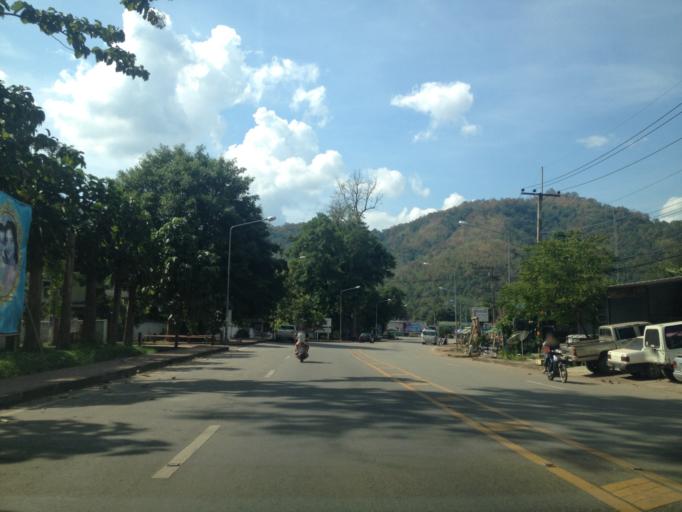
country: TH
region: Chiang Mai
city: Samoeng
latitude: 18.8475
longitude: 98.7337
